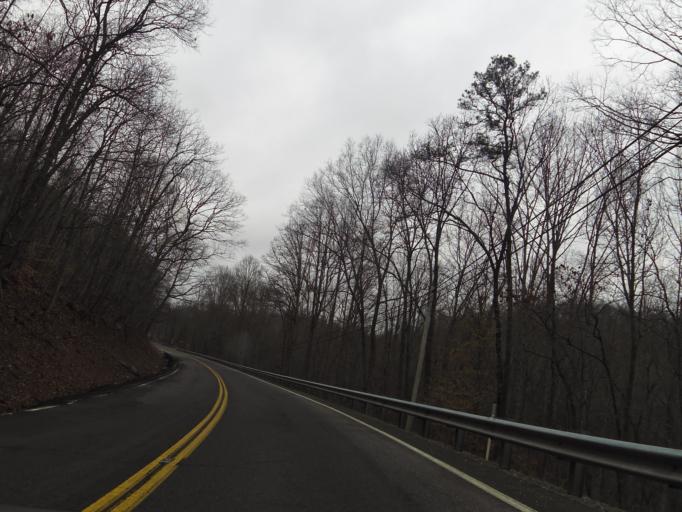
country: US
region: Tennessee
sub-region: Morgan County
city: Wartburg
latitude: 36.1546
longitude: -84.6439
